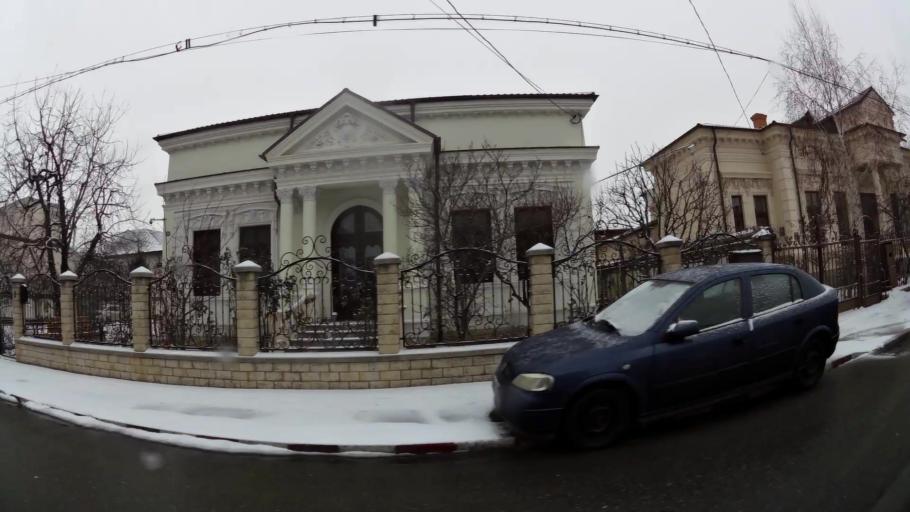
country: RO
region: Dambovita
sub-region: Municipiul Targoviste
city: Targoviste
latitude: 44.9288
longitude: 25.4560
